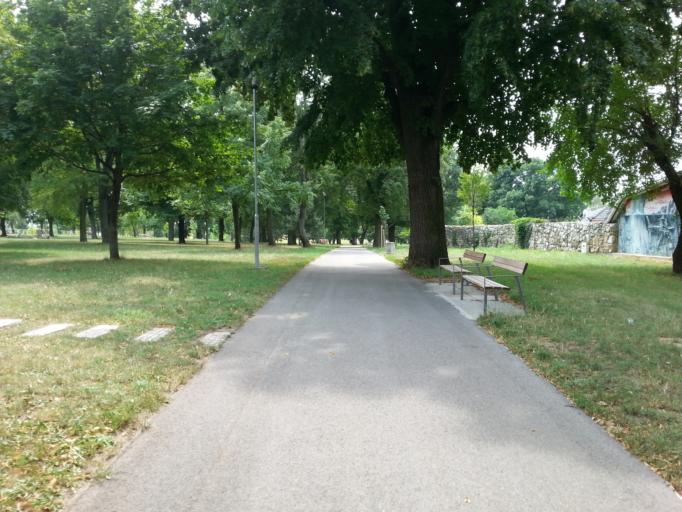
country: SK
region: Trenciansky
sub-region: Okres Nove Mesto nad Vahom
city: Nove Mesto nad Vahom
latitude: 48.7543
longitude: 17.8282
